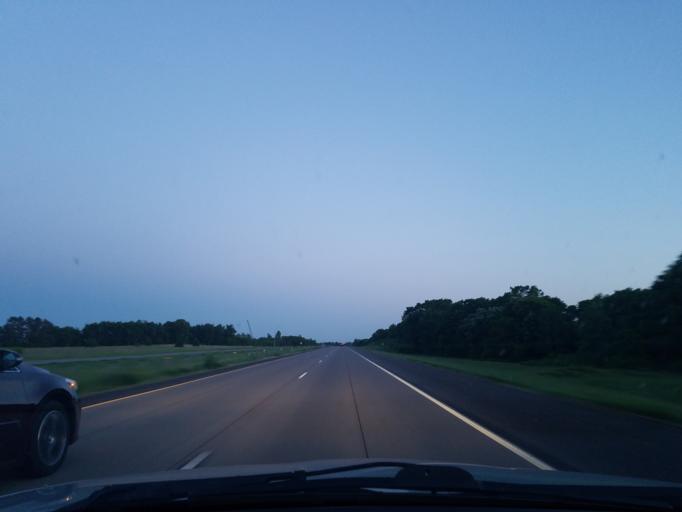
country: US
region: Minnesota
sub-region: Chisago County
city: Harris
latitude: 45.6066
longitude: -92.9941
